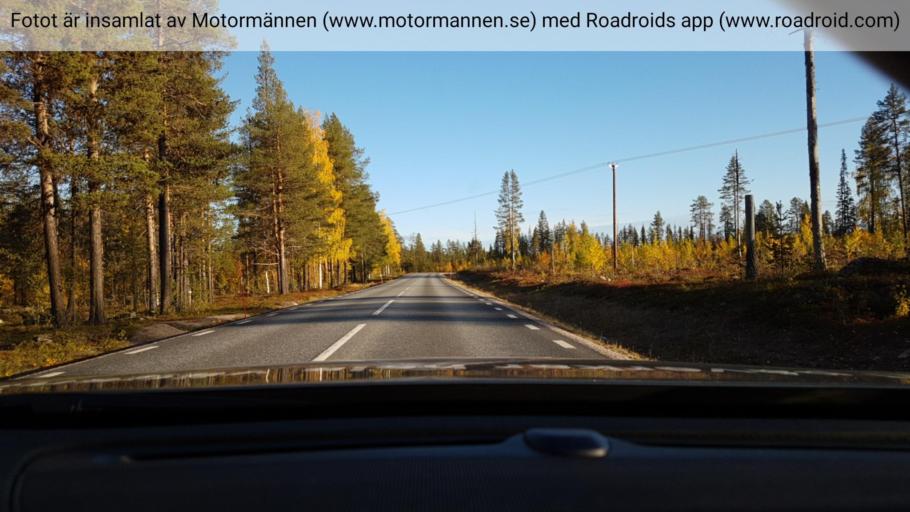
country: SE
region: Norrbotten
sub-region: Jokkmokks Kommun
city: Jokkmokk
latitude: 66.7977
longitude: 19.8776
